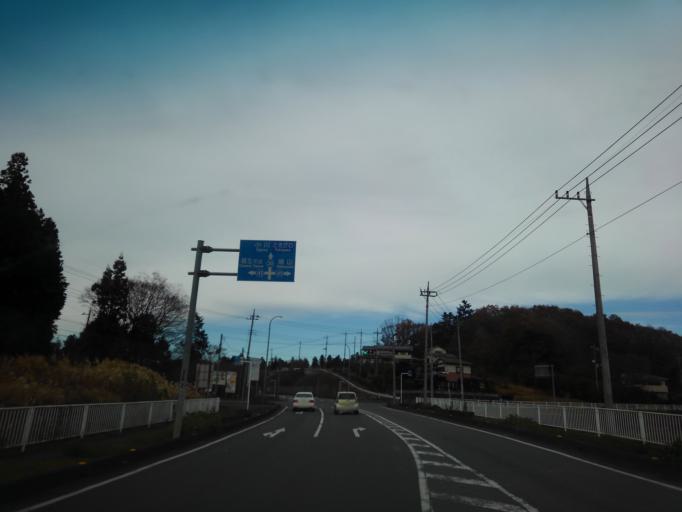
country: JP
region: Saitama
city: Morohongo
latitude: 35.9731
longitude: 139.2991
